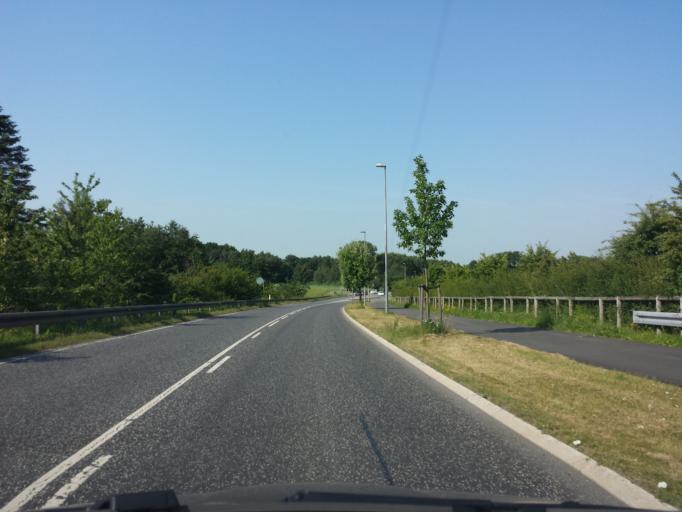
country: DK
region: Capital Region
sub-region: Ballerup Kommune
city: Malov
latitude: 55.7427
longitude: 12.3255
